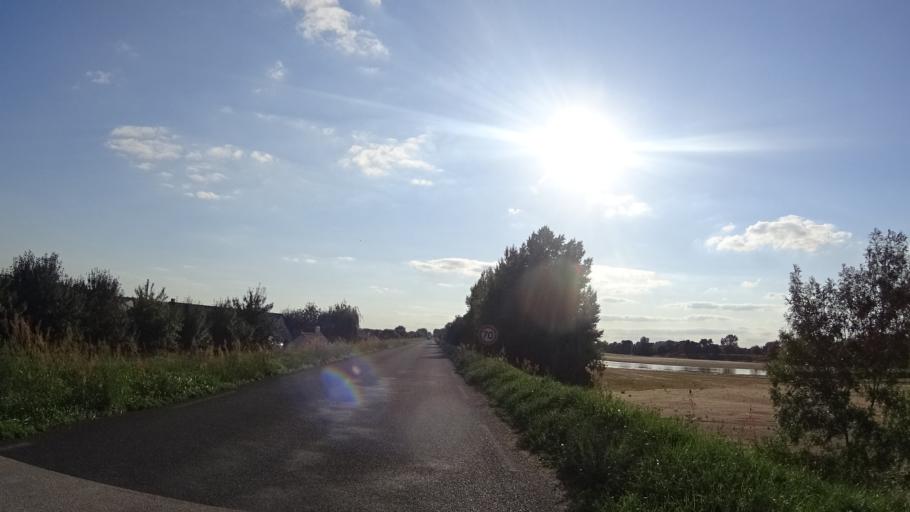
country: FR
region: Pays de la Loire
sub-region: Departement de Maine-et-Loire
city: Le Mesnil-en-Vallee
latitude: 47.3842
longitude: -0.9360
